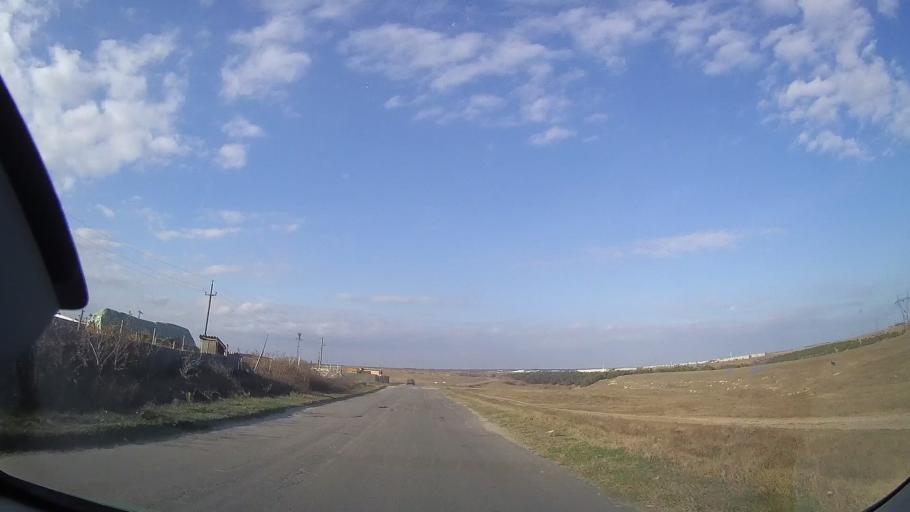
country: RO
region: Constanta
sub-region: Comuna Limanu
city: Limanu
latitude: 43.8034
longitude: 28.5213
